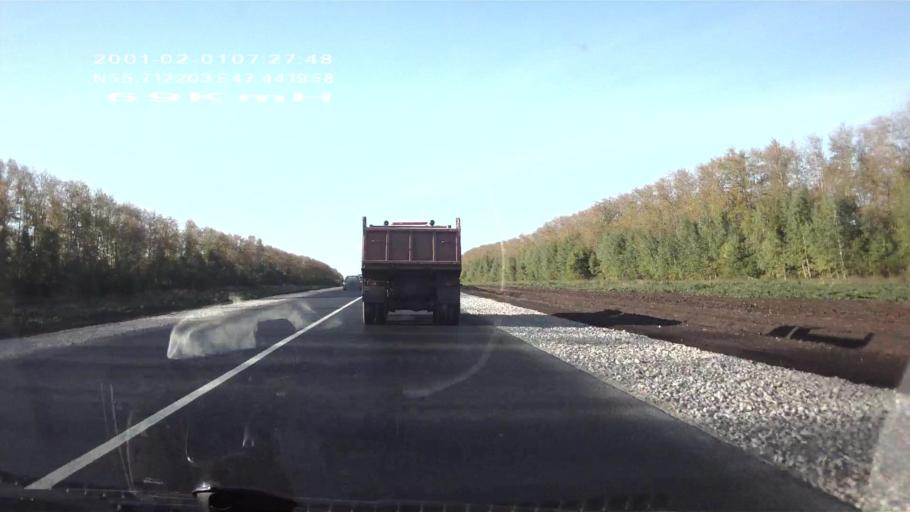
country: RU
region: Chuvashia
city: Shikhazany
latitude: 55.7119
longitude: 47.4418
